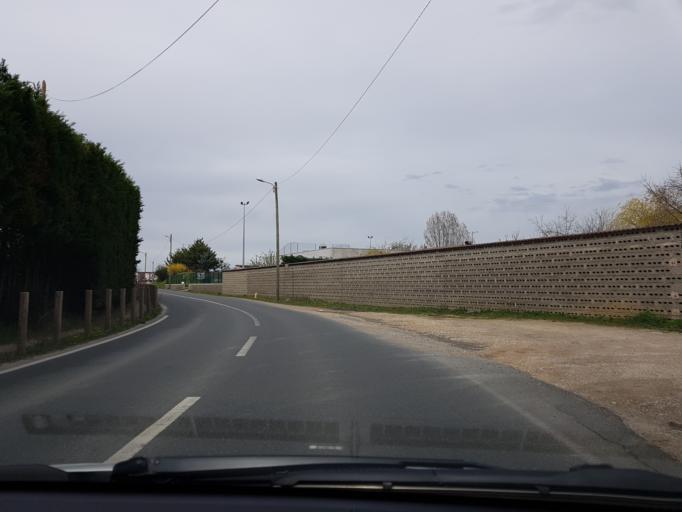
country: FR
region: Rhone-Alpes
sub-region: Departement de l'Ain
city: Jassans-Riottier
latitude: 45.9826
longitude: 4.7535
